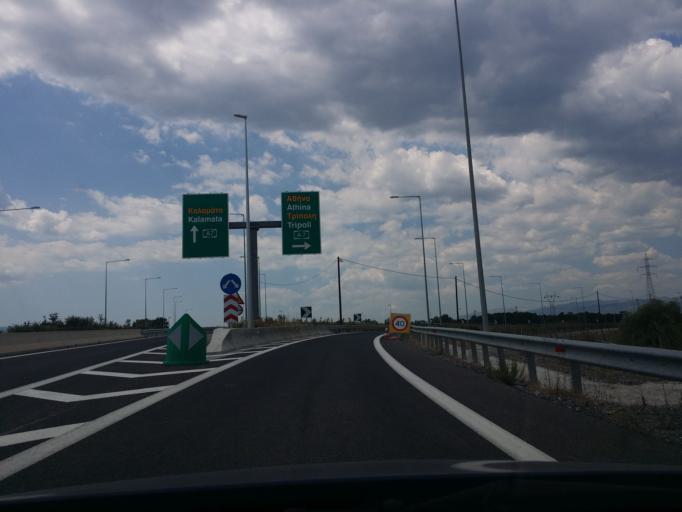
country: GR
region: Peloponnese
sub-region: Nomos Arkadias
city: Megalopoli
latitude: 37.3587
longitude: 22.1490
